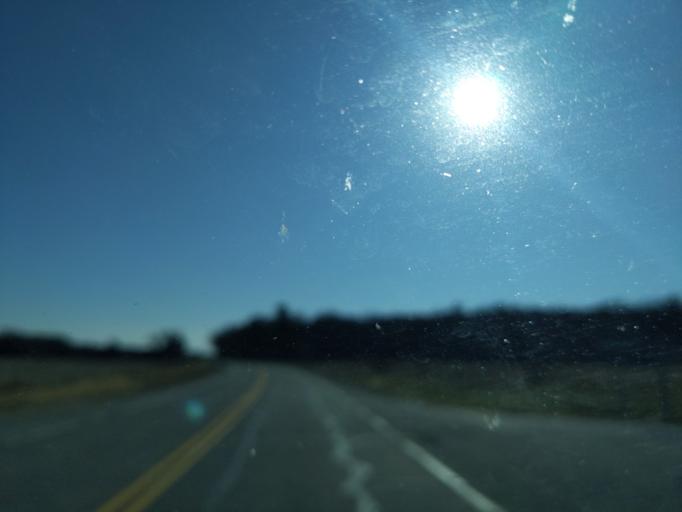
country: US
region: Wisconsin
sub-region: Waushara County
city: Wautoma
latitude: 44.0904
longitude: -89.2925
